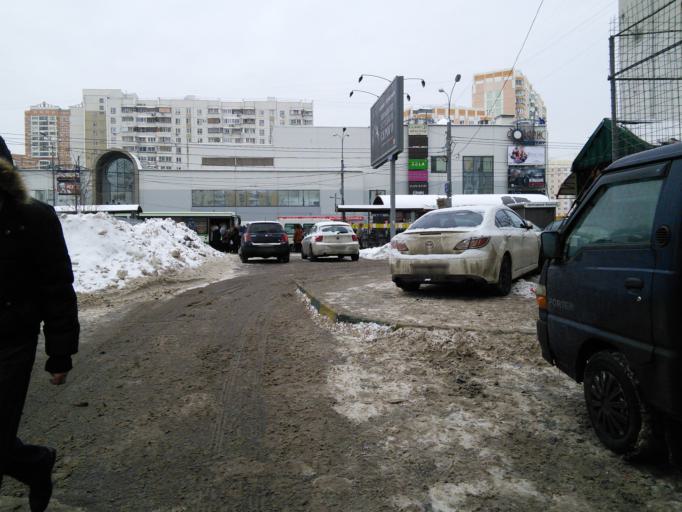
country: RU
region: Moscow
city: Lyublino
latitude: 55.6596
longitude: 37.7521
